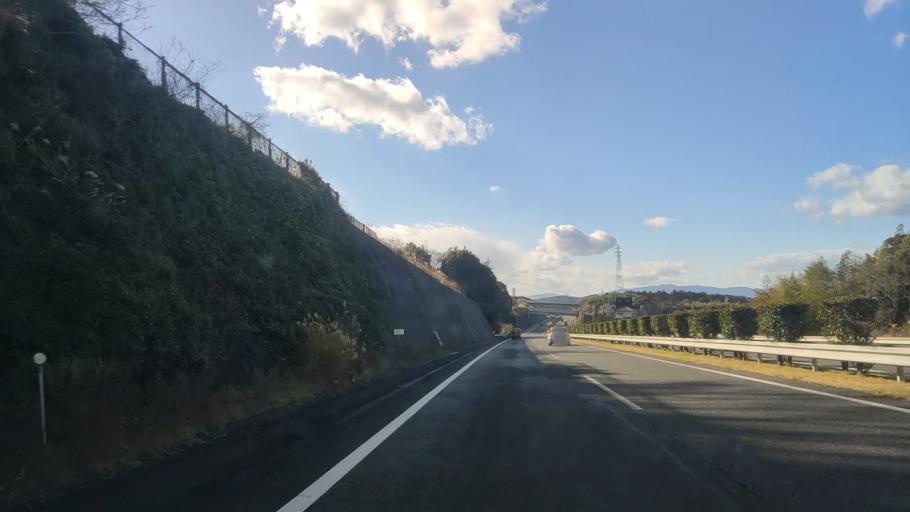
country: JP
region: Ehime
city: Niihama
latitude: 33.9146
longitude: 133.2806
